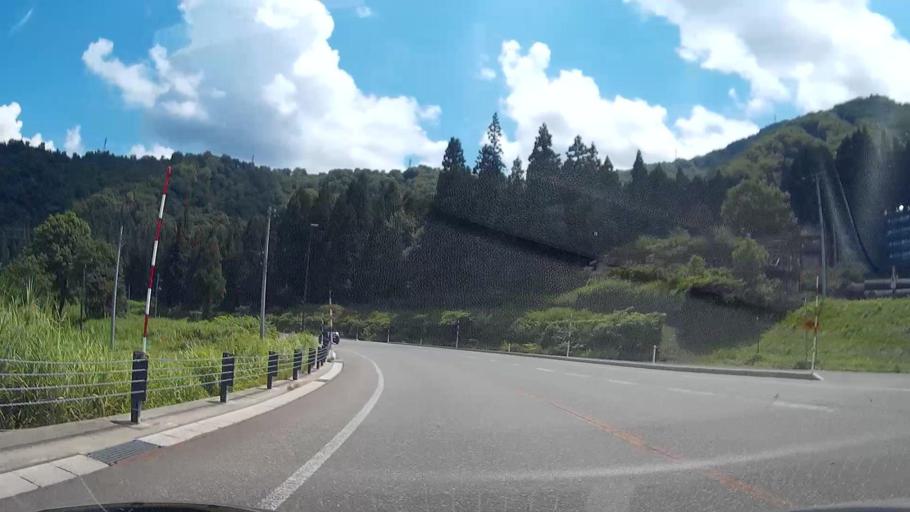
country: JP
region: Niigata
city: Shiozawa
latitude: 36.9091
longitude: 138.7971
